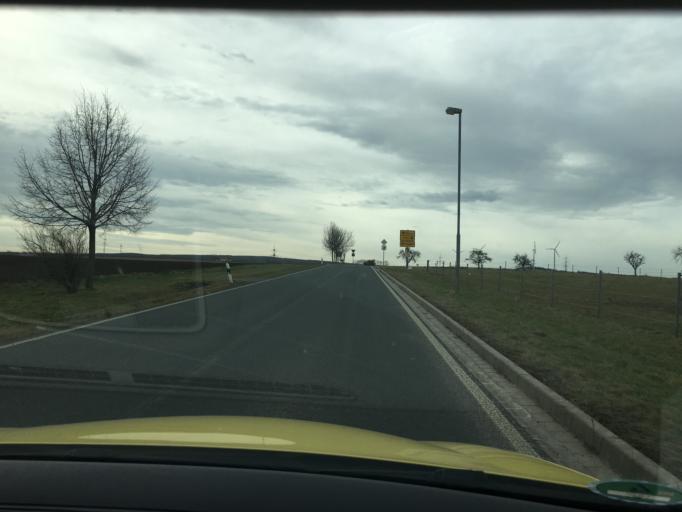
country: DE
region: Thuringia
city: Ballstedt
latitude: 51.0531
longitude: 11.2142
